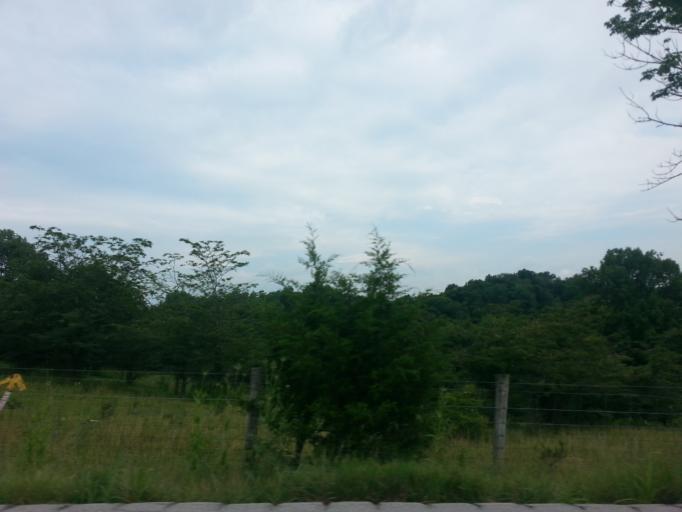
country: US
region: Kentucky
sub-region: Robertson County
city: Mount Olivet
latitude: 38.5210
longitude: -84.0625
